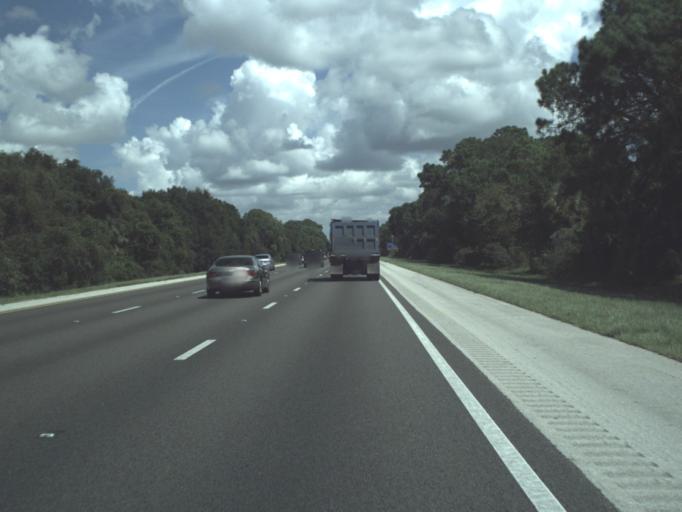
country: US
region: Florida
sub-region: Sarasota County
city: Vamo
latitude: 27.2399
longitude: -82.4512
